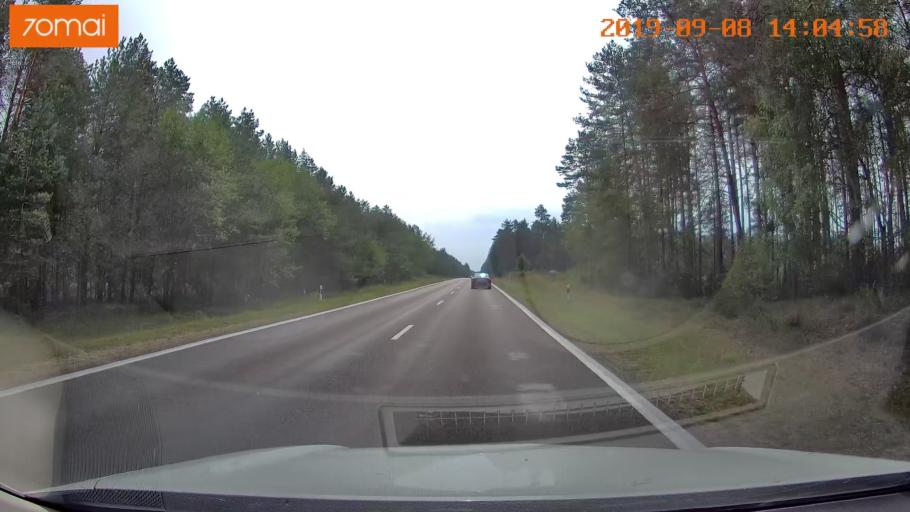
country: LT
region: Alytaus apskritis
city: Druskininkai
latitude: 54.0900
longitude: 24.1975
